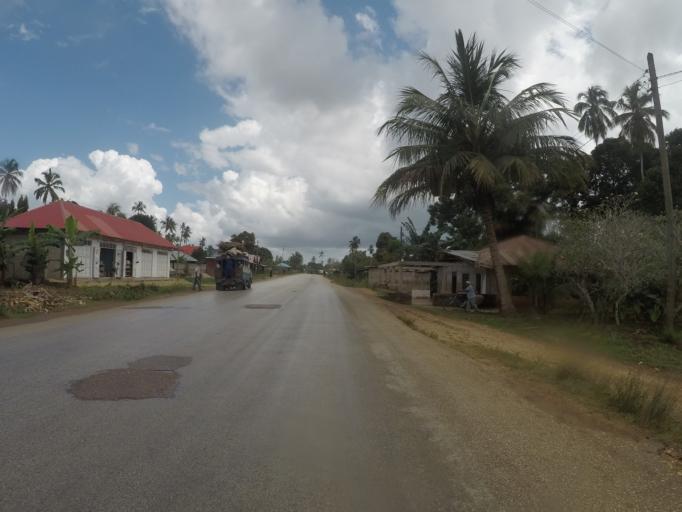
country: TZ
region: Zanzibar Central/South
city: Koani
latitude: -6.0467
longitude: 39.2271
